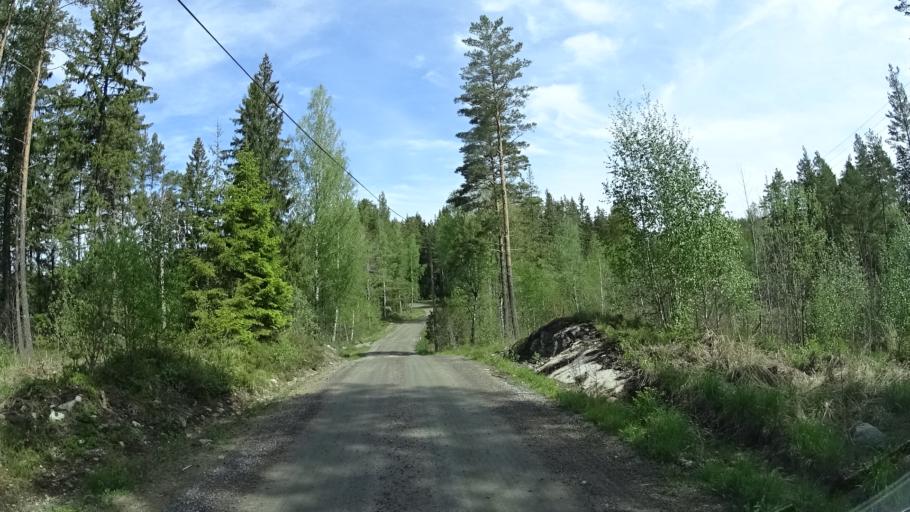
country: SE
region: OEstergoetland
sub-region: Finspangs Kommun
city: Finspang
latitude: 58.7556
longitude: 15.8355
